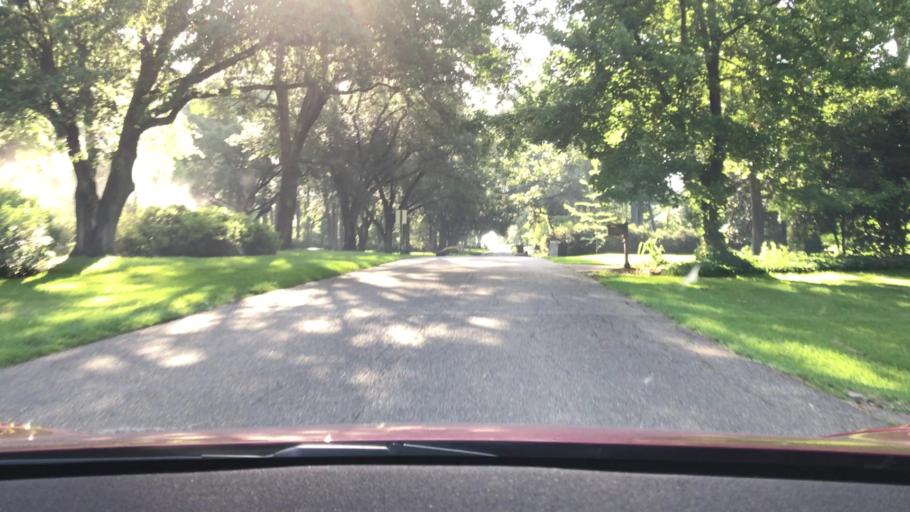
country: US
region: Louisiana
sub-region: Bossier Parish
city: Bossier City
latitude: 32.4565
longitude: -93.7428
